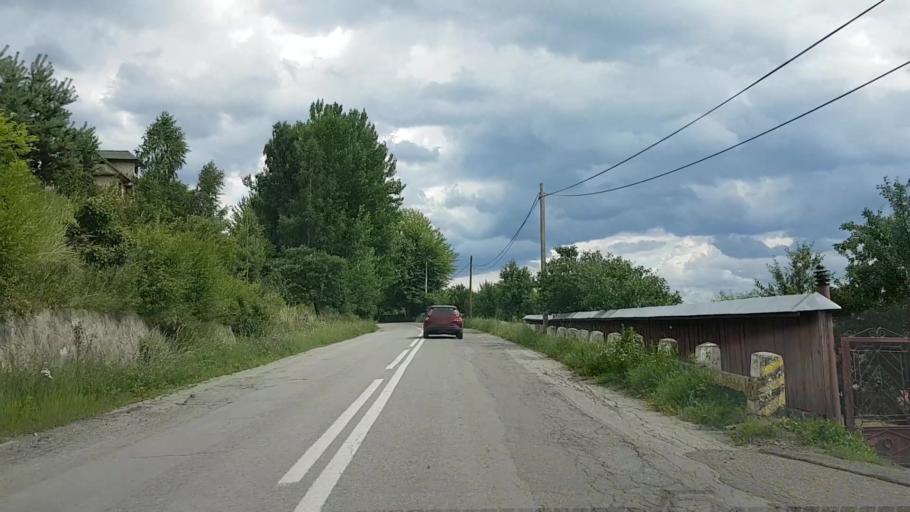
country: RO
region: Neamt
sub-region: Comuna Hangu
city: Hangu
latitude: 47.0463
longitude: 26.0415
